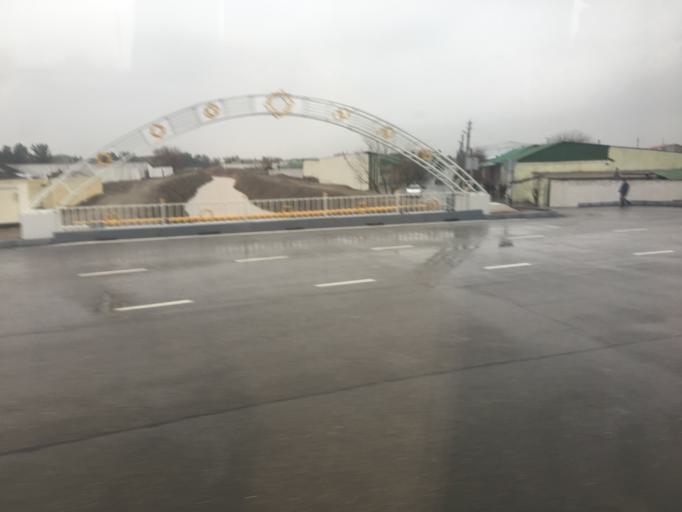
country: TM
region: Lebap
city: Turkmenabat
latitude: 39.0282
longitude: 63.5958
